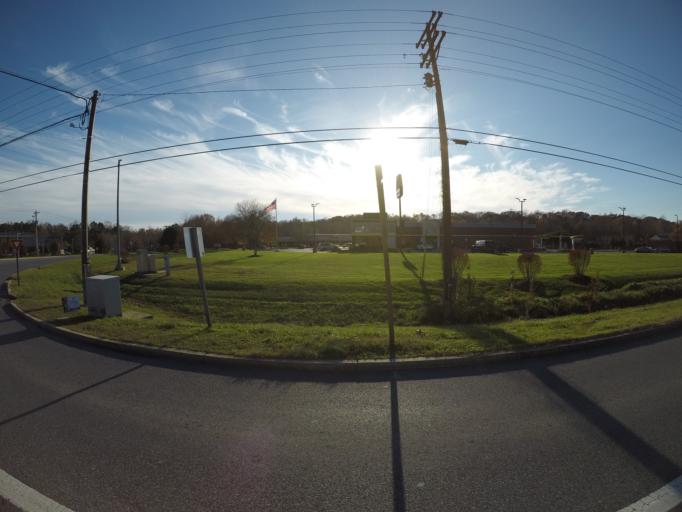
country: US
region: Maryland
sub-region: Saint Mary's County
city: Leonardtown
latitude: 38.3054
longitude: -76.6588
